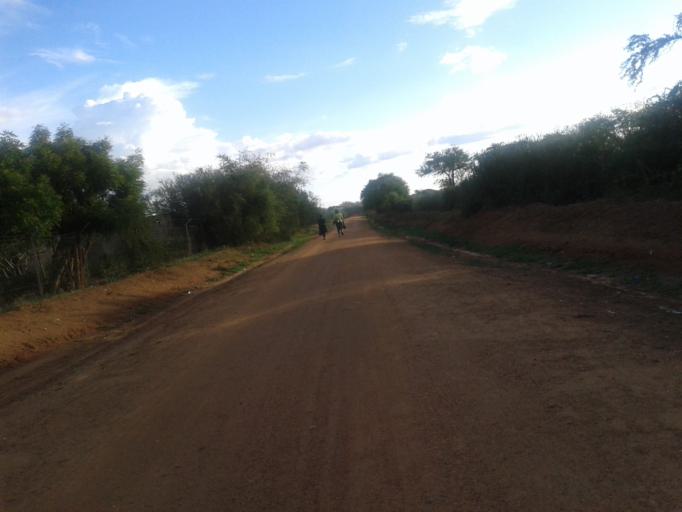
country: UG
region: Northern Region
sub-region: Kotido District
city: Kotido
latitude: 3.0000
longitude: 34.1060
